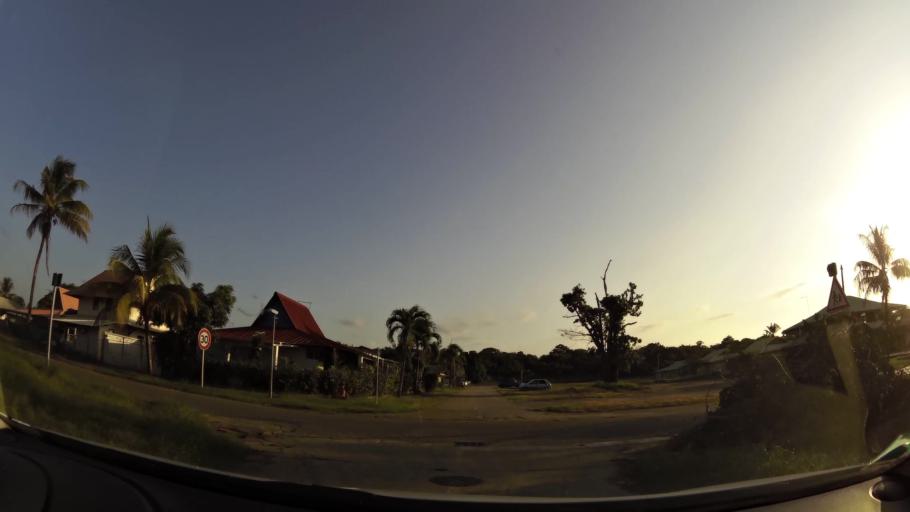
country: GF
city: Macouria
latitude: 5.0169
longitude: -52.4792
